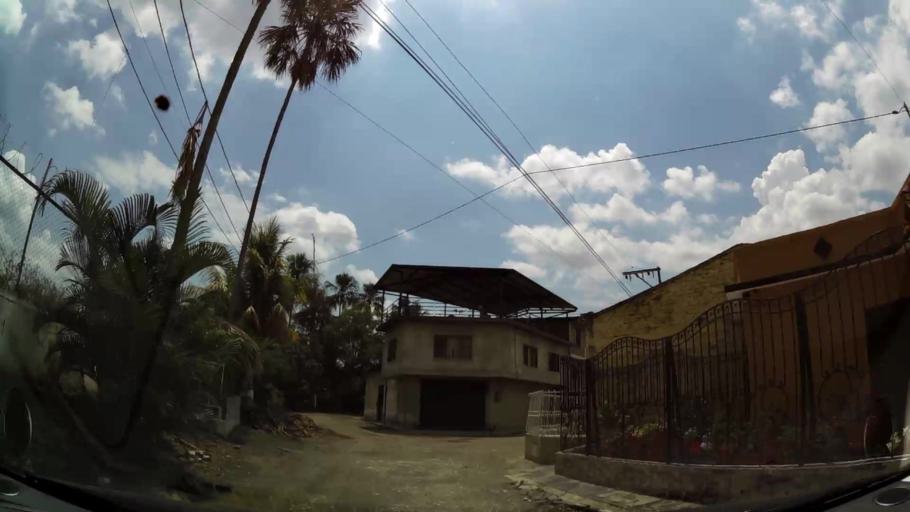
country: CO
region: Valle del Cauca
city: Cali
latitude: 3.4542
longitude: -76.4739
